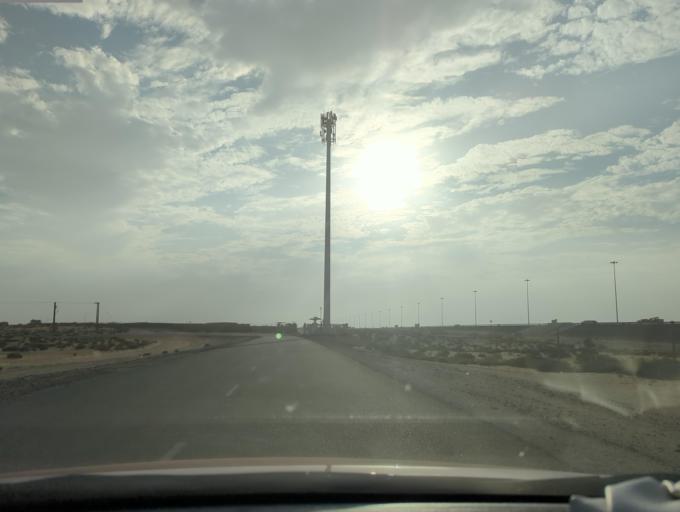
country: AE
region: Dubai
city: Dubai
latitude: 24.7230
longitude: 54.8697
